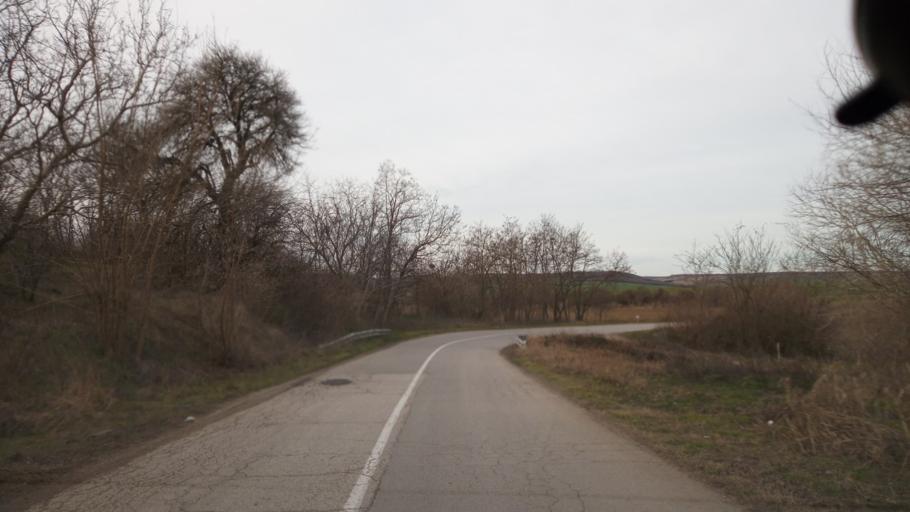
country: BG
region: Pleven
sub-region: Obshtina Belene
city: Belene
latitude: 43.6206
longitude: 25.0646
